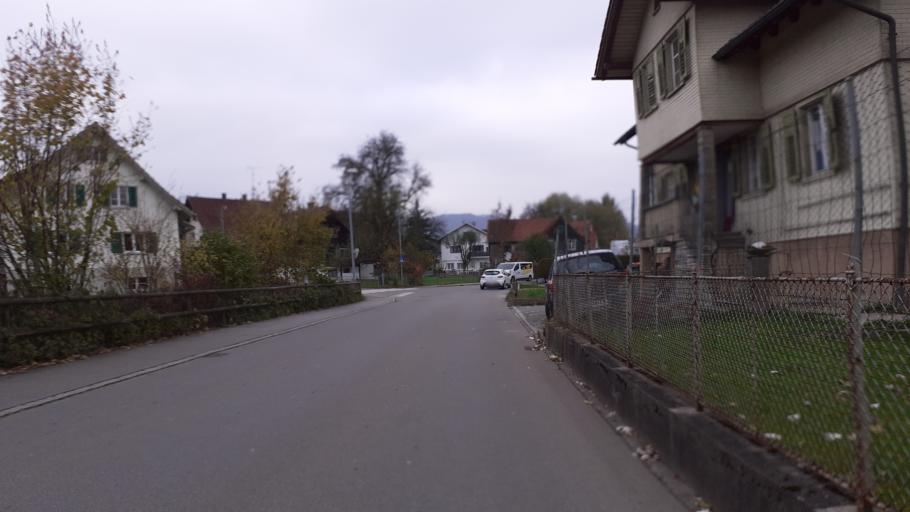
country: AT
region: Vorarlberg
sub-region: Politischer Bezirk Dornbirn
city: Lustenau
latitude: 47.4247
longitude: 9.6653
